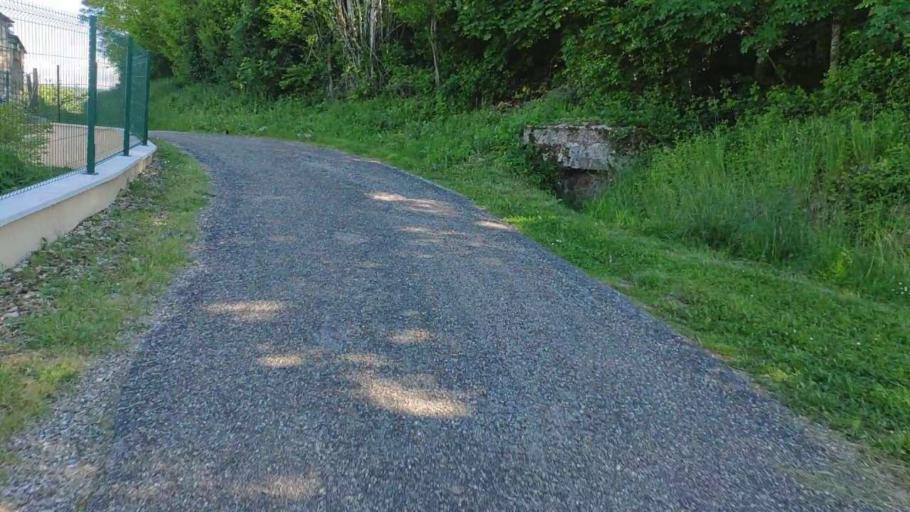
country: FR
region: Franche-Comte
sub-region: Departement du Jura
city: Perrigny
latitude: 46.7153
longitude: 5.5773
